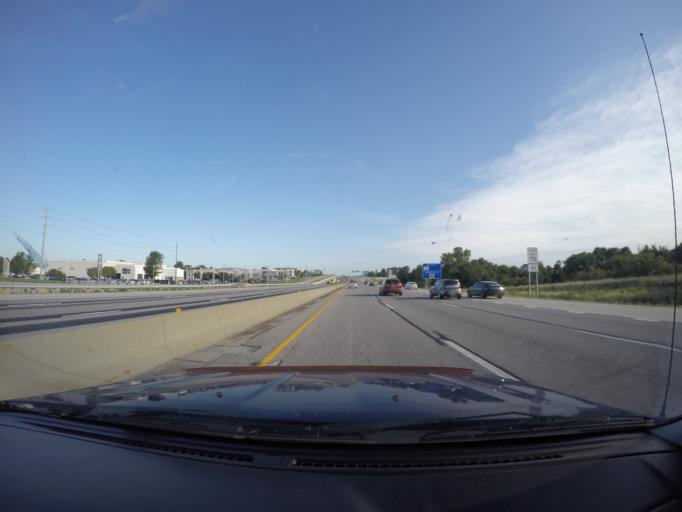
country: US
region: Missouri
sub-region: Platte County
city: Weatherby Lake
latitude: 39.2656
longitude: -94.6637
